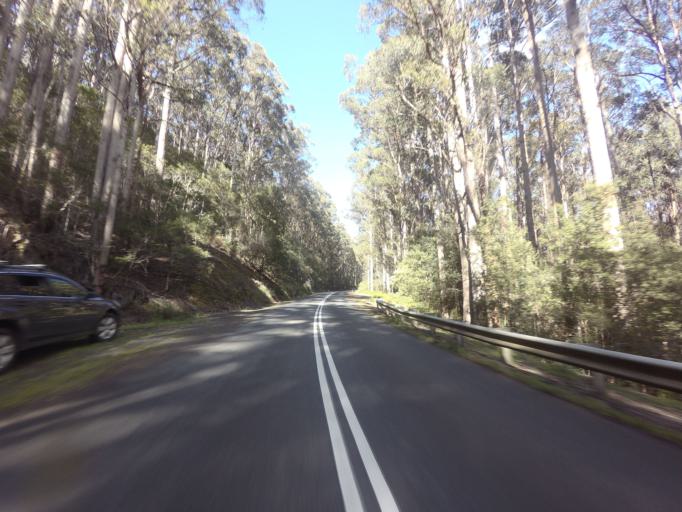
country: AU
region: Tasmania
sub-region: Derwent Valley
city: New Norfolk
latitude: -42.7382
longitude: 146.6638
